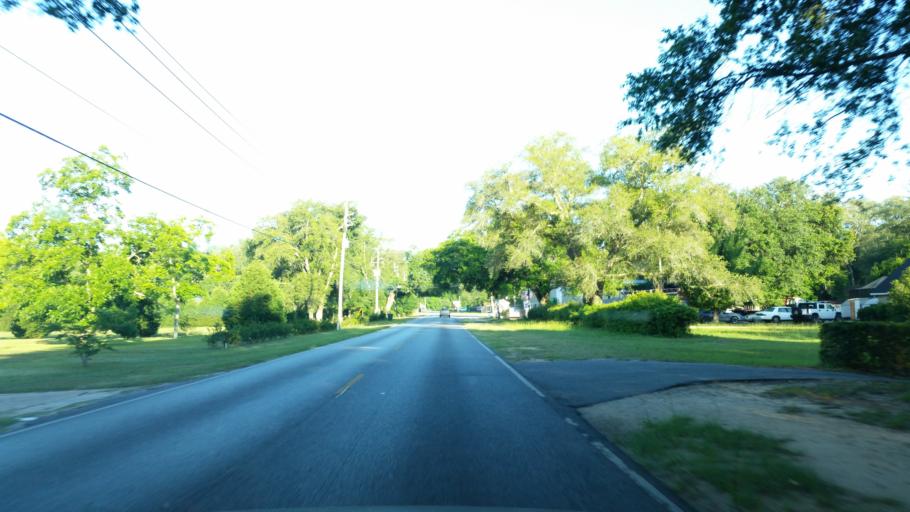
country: US
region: Florida
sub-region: Escambia County
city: Bellview
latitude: 30.4492
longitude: -87.3131
